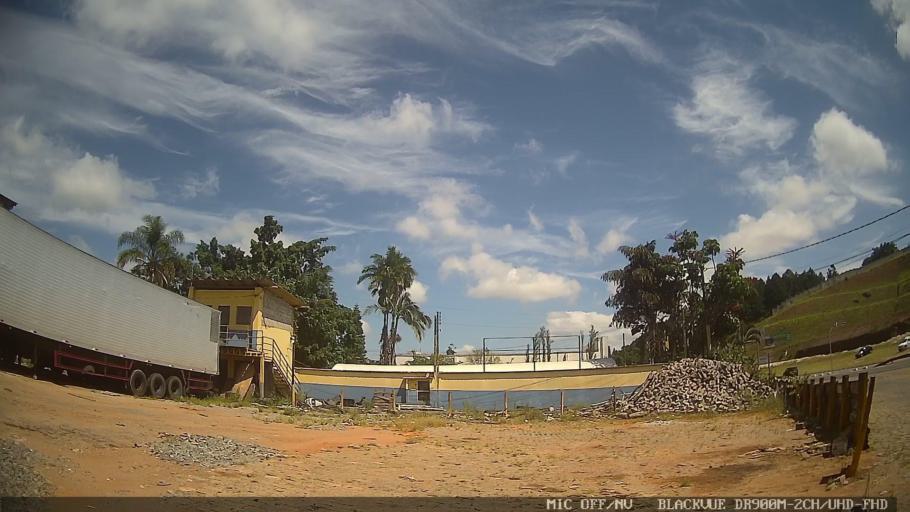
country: BR
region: Sao Paulo
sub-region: Braganca Paulista
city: Braganca Paulista
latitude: -22.9950
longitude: -46.5640
